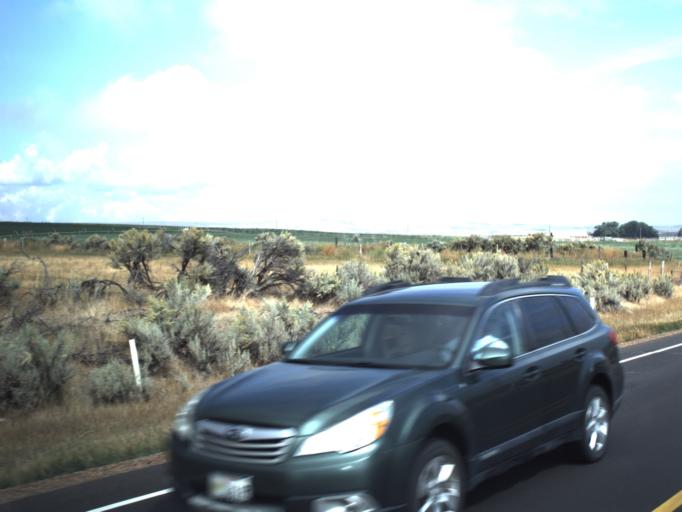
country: US
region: Utah
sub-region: Rich County
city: Randolph
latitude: 41.7021
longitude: -111.1611
